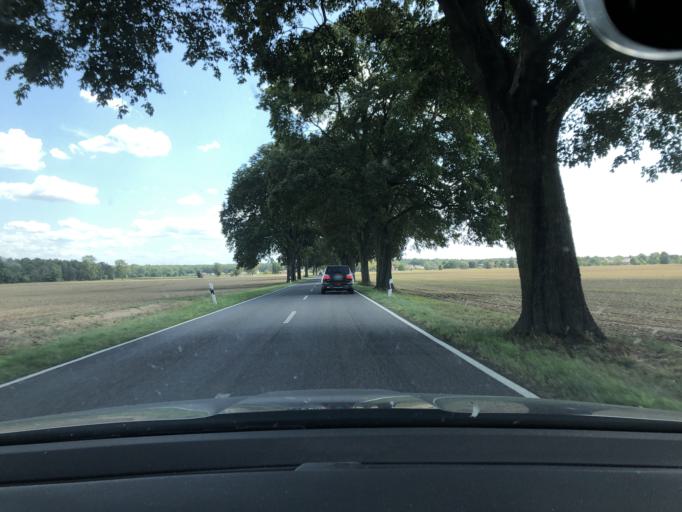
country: DE
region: Brandenburg
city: Ruthnick
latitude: 52.8888
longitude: 12.9913
